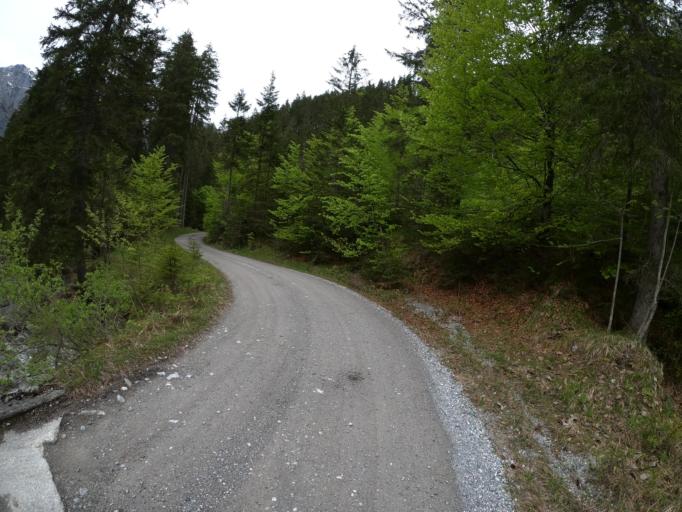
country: AT
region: Salzburg
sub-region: Politischer Bezirk Sankt Johann im Pongau
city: Werfen
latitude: 47.4664
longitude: 13.0823
